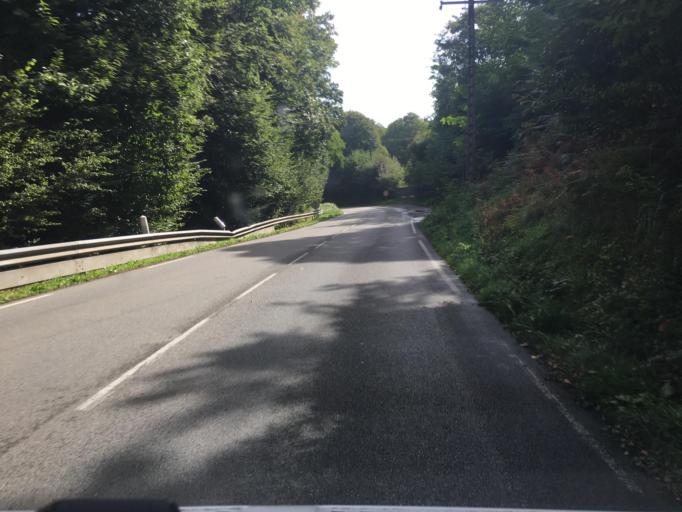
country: FR
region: Brittany
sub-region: Departement du Finistere
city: La Foret-Fouesnant
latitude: 47.9170
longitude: -3.9703
